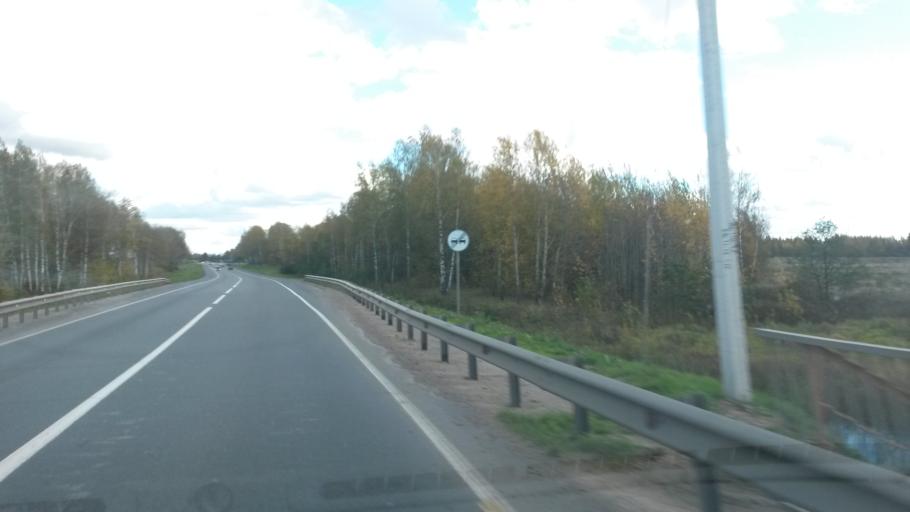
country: RU
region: Jaroslavl
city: Tunoshna
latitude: 57.5377
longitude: 40.0112
